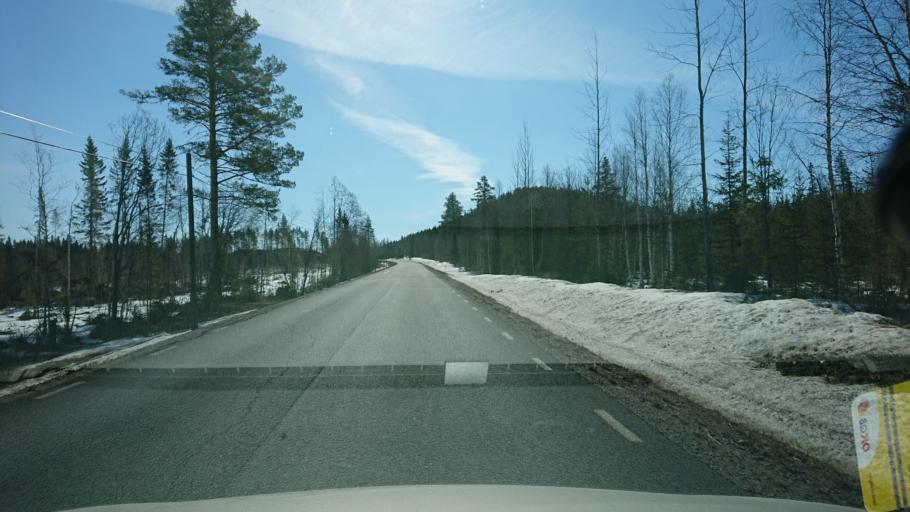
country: SE
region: Vaesterbotten
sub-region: Dorotea Kommun
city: Dorotea
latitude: 64.1044
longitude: 16.2416
